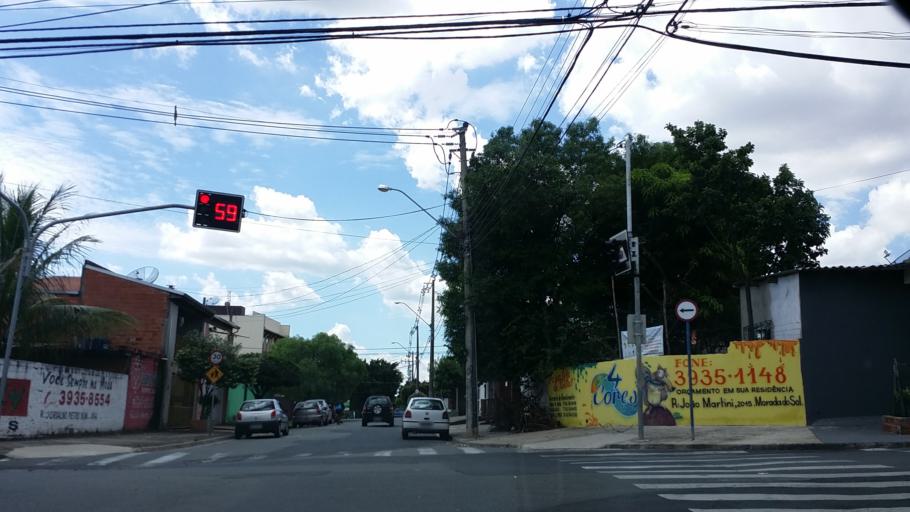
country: BR
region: Sao Paulo
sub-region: Indaiatuba
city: Indaiatuba
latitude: -23.1211
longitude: -47.2463
